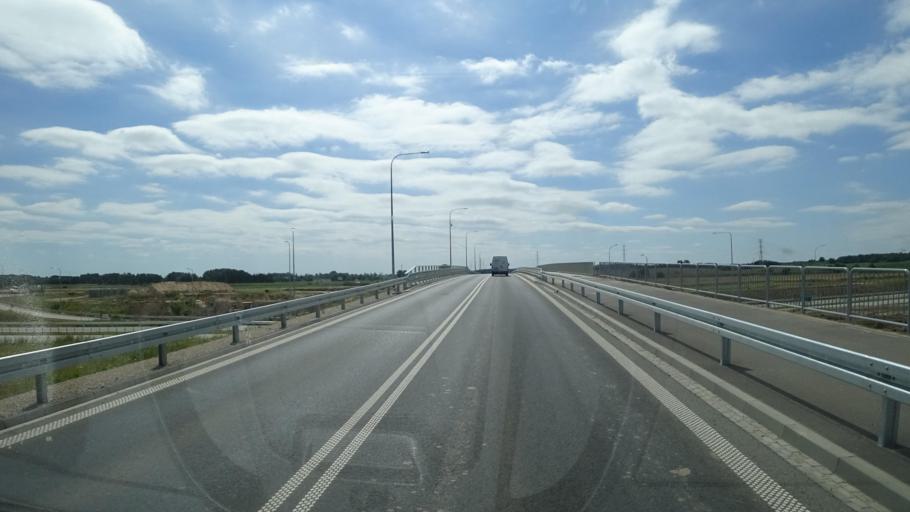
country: PL
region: Warmian-Masurian Voivodeship
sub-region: Powiat elcki
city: Elk
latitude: 53.7564
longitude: 22.3389
